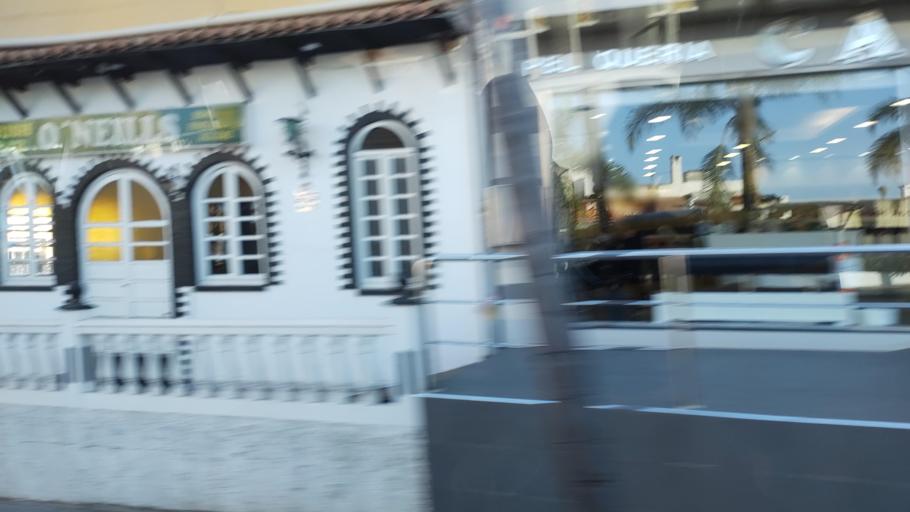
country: ES
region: Andalusia
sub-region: Provincia de Malaga
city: Torremolinos
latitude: 36.6316
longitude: -4.4938
